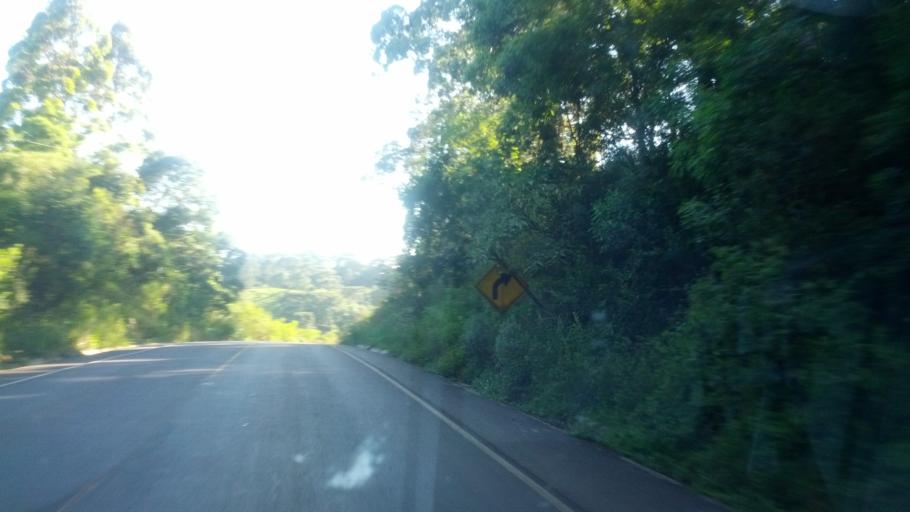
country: BR
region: Santa Catarina
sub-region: Lages
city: Lages
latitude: -27.9251
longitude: -50.5464
